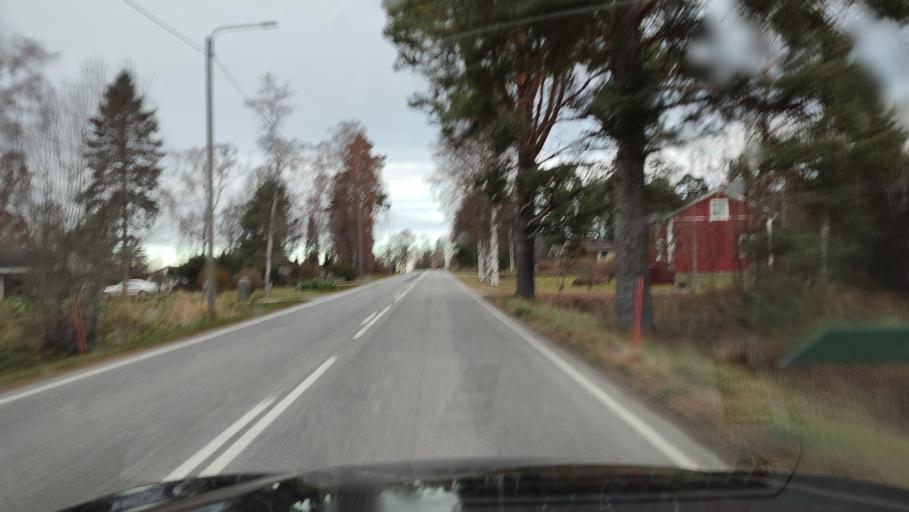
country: FI
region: Ostrobothnia
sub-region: Sydosterbotten
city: Naerpes
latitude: 62.4205
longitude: 21.3426
